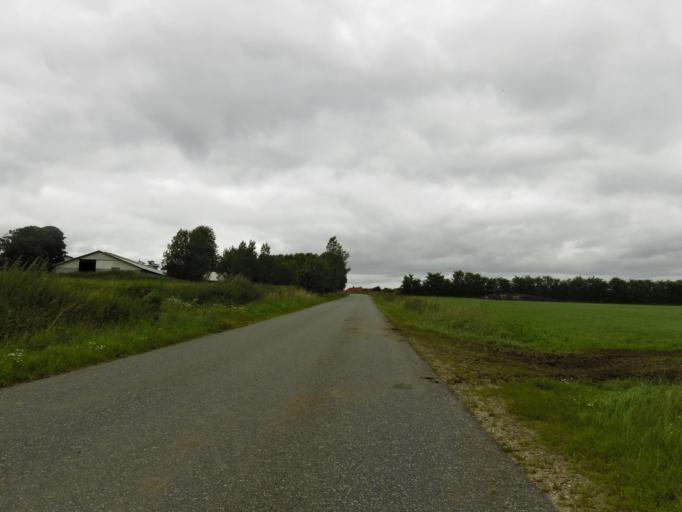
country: DK
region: South Denmark
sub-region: Haderslev Kommune
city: Gram
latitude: 55.2655
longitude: 9.1672
